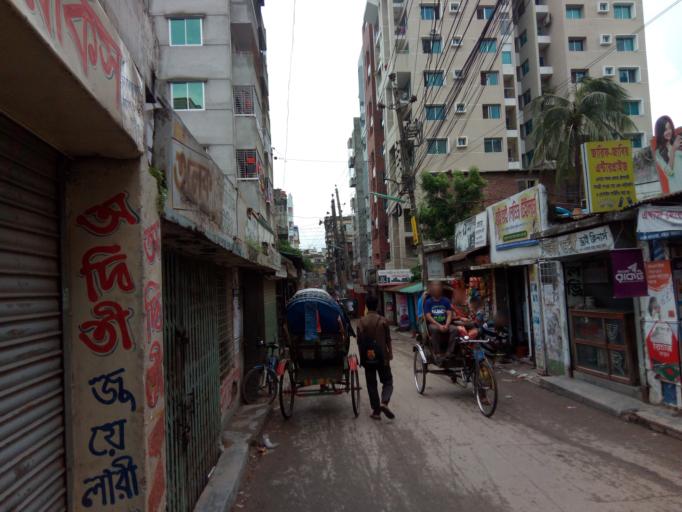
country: BD
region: Dhaka
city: Azimpur
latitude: 23.7499
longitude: 90.3633
